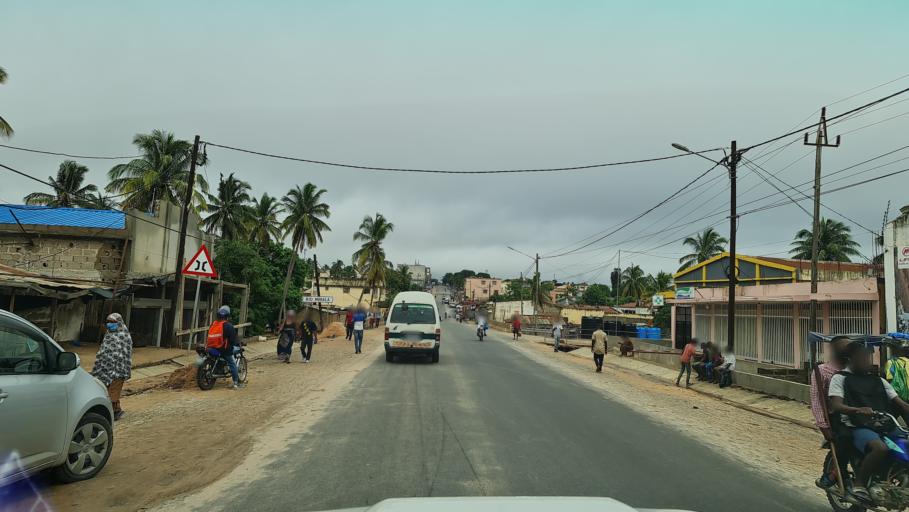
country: MZ
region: Nampula
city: Nampula
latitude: -15.1325
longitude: 39.2714
